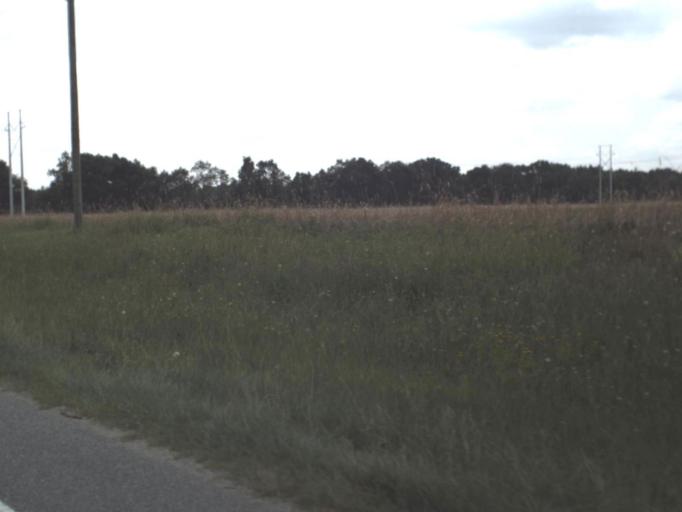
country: US
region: Florida
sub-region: Madison County
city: Madison
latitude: 30.4866
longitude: -83.2195
